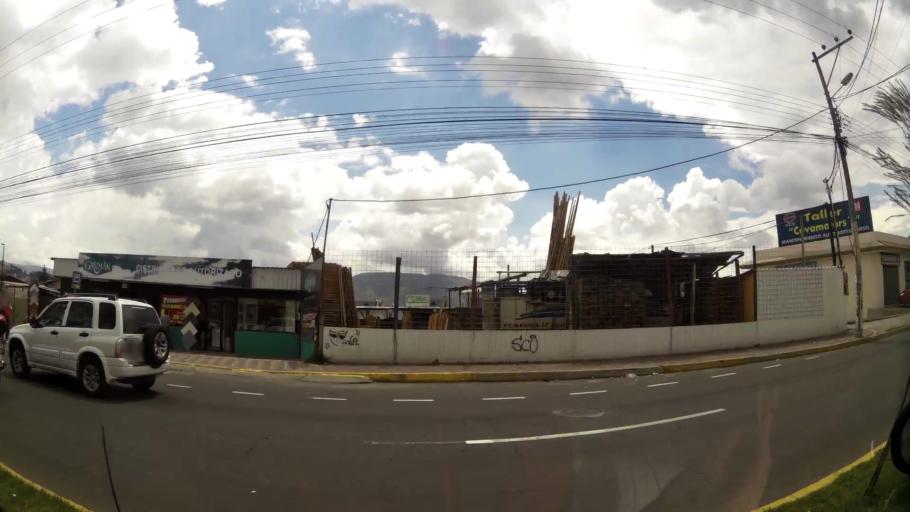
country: EC
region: Pichincha
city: Quito
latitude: -0.0978
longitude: -78.4430
